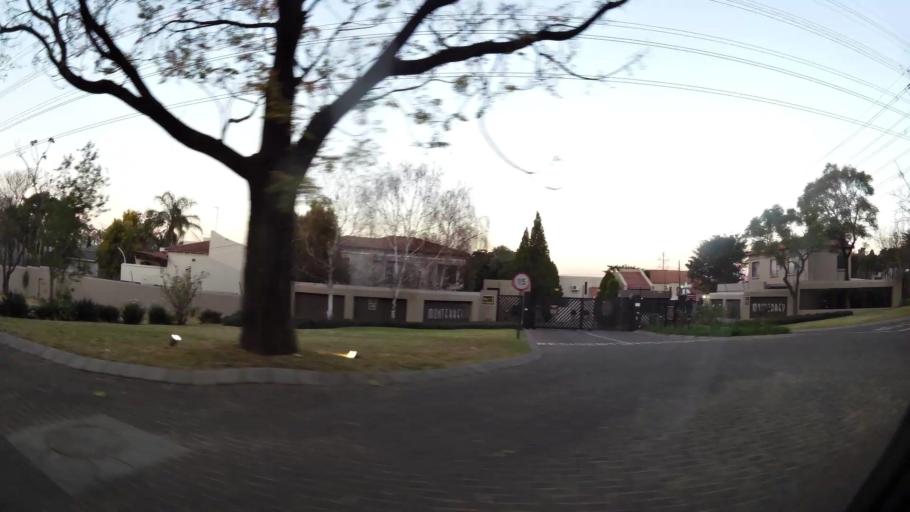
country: ZA
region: Gauteng
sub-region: City of Johannesburg Metropolitan Municipality
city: Diepsloot
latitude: -26.0297
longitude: 28.0238
